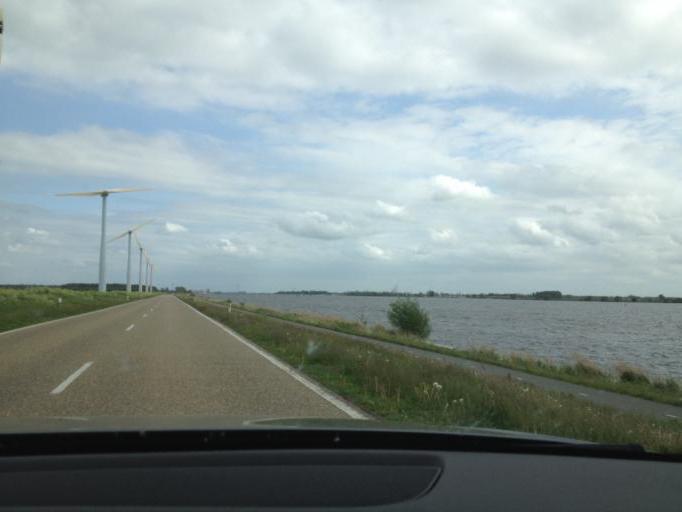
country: NL
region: Utrecht
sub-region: Gemeente Bunschoten
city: Spakenburg
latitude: 52.2784
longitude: 5.3612
